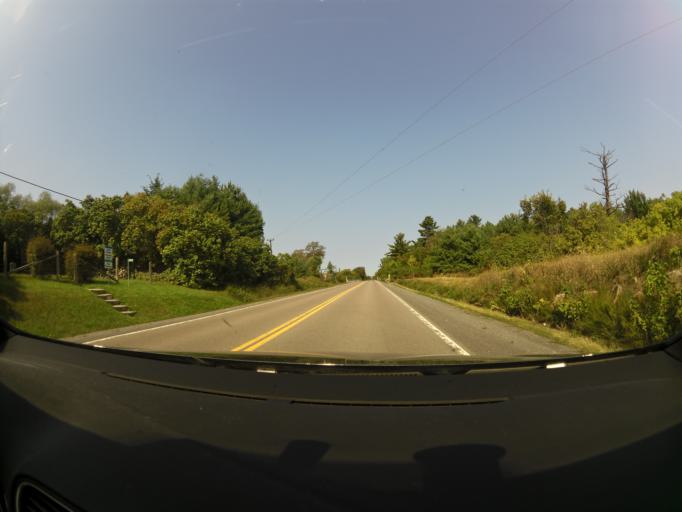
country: CA
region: Ontario
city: Arnprior
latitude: 45.4398
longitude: -76.1795
